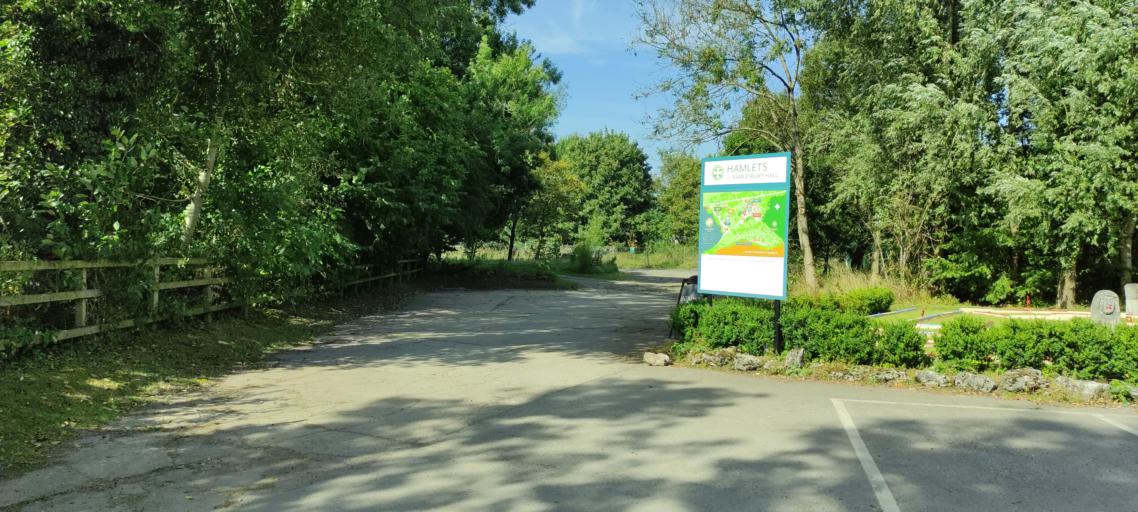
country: GB
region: England
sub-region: Lancashire
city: Longridge
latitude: 53.7706
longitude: -2.5707
